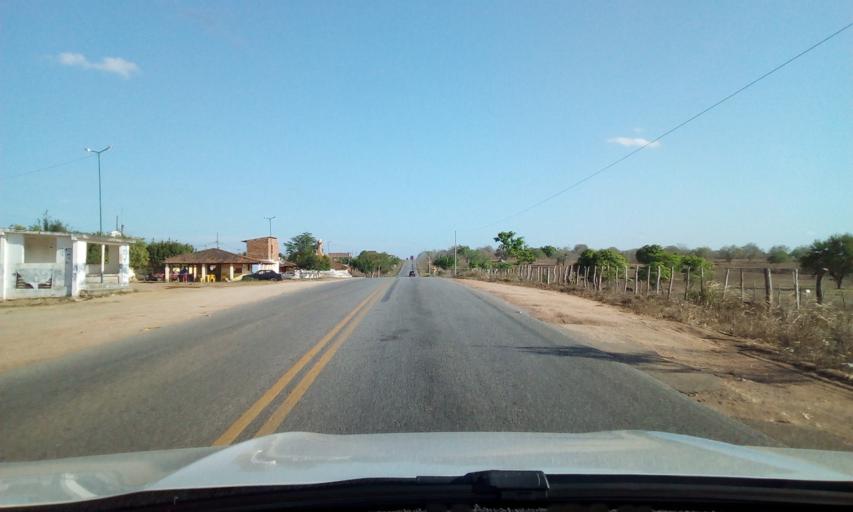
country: BR
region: Paraiba
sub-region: Mulungu
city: Mulungu
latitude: -6.9579
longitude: -35.4140
